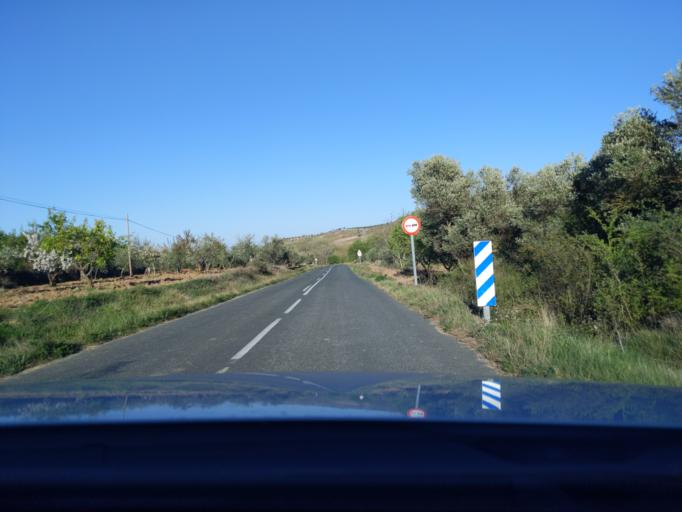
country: ES
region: La Rioja
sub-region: Provincia de La Rioja
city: Bergasa
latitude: 42.2558
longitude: -2.1185
